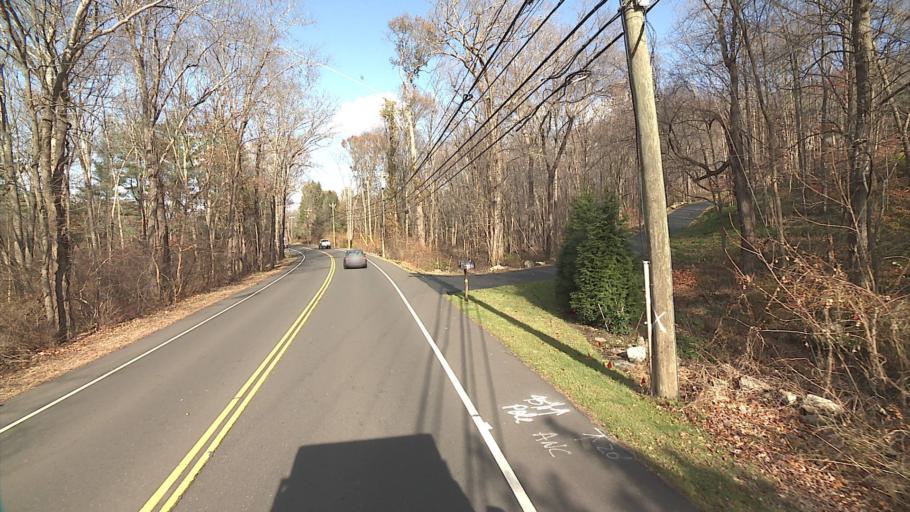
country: US
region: Connecticut
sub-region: Fairfield County
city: Wilton
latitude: 41.2194
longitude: -73.3839
